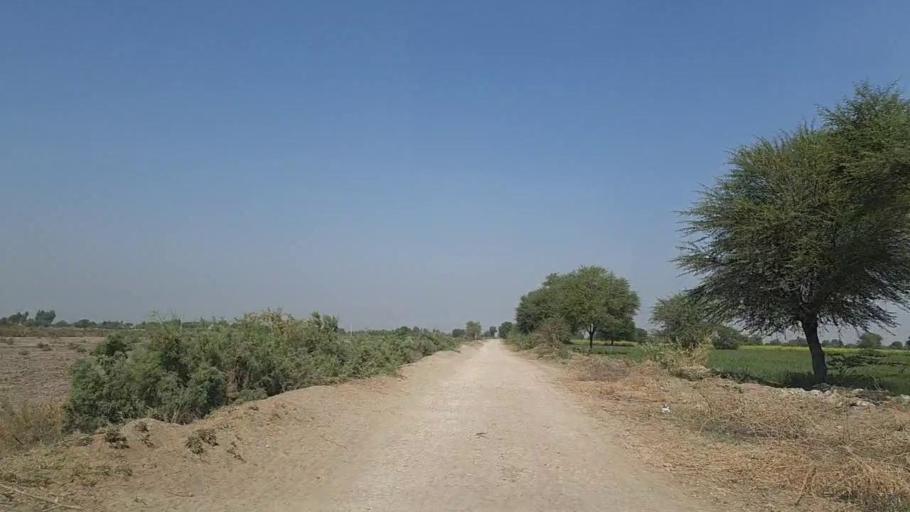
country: PK
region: Sindh
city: Samaro
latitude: 25.2100
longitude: 69.4042
